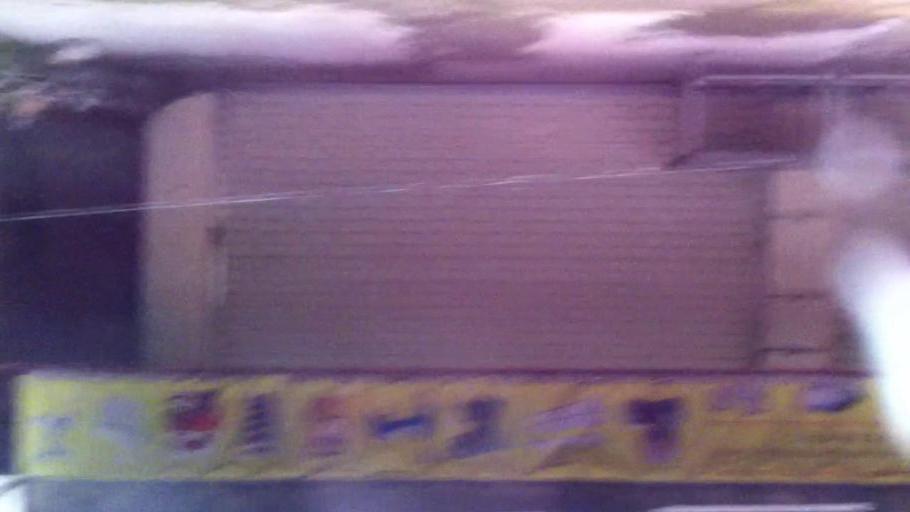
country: PH
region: Cordillera
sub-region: Province of Benguet
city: La Trinidad
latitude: 16.4418
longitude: 120.5930
